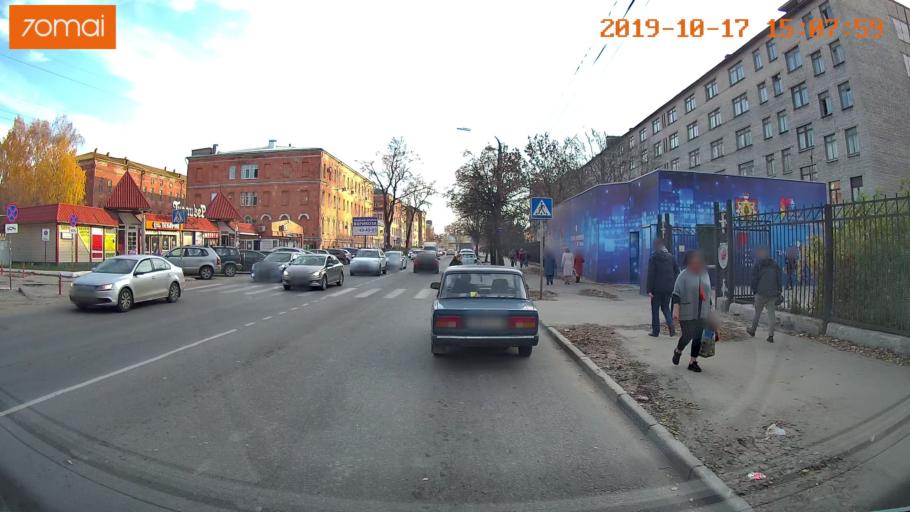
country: RU
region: Rjazan
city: Ryazan'
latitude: 54.6321
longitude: 39.7241
